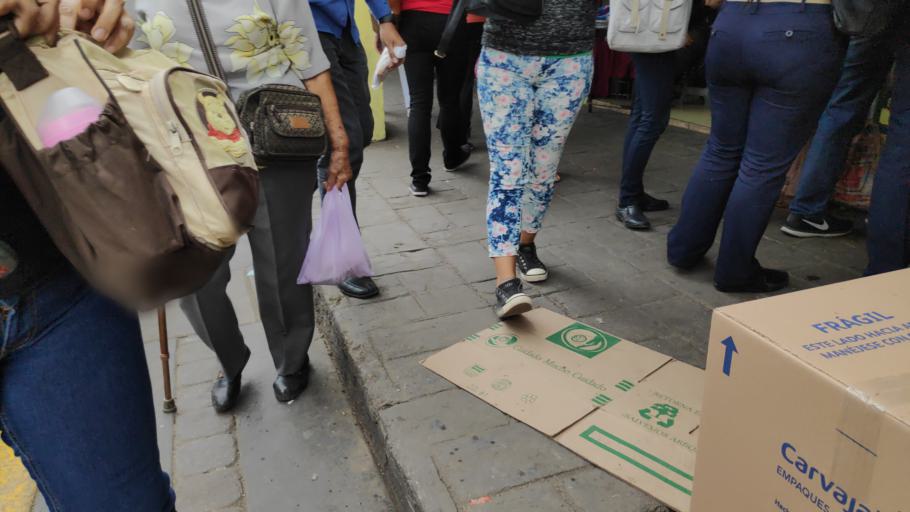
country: MX
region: Sinaloa
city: Culiacan
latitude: 24.8081
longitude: -107.3966
